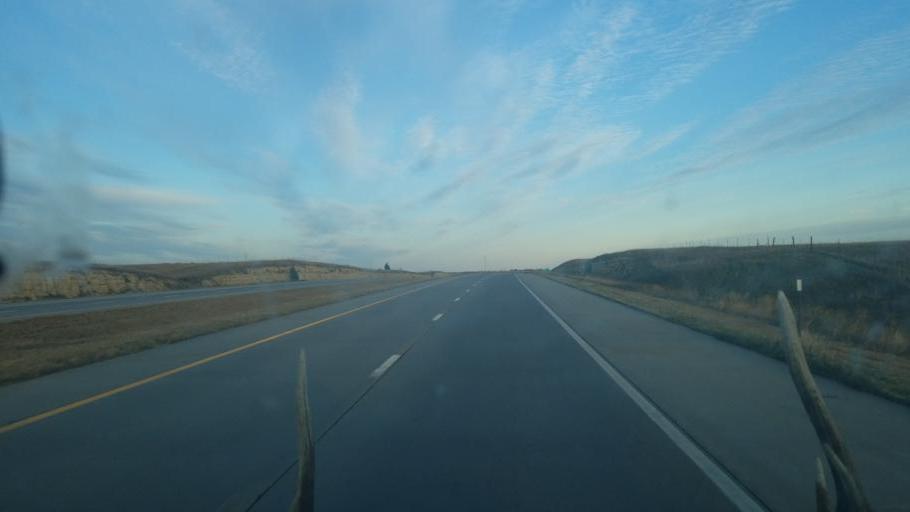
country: US
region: Kansas
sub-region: Riley County
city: Manhattan
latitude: 39.0660
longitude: -96.5861
